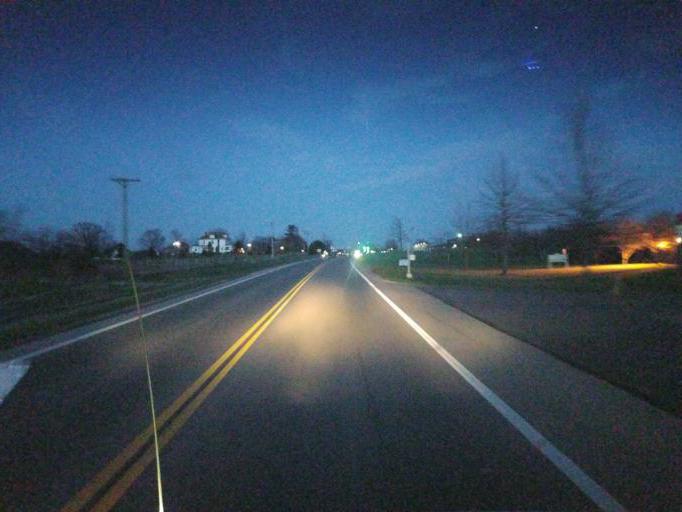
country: US
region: Ohio
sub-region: Logan County
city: Bellefontaine
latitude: 40.3635
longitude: -83.7977
